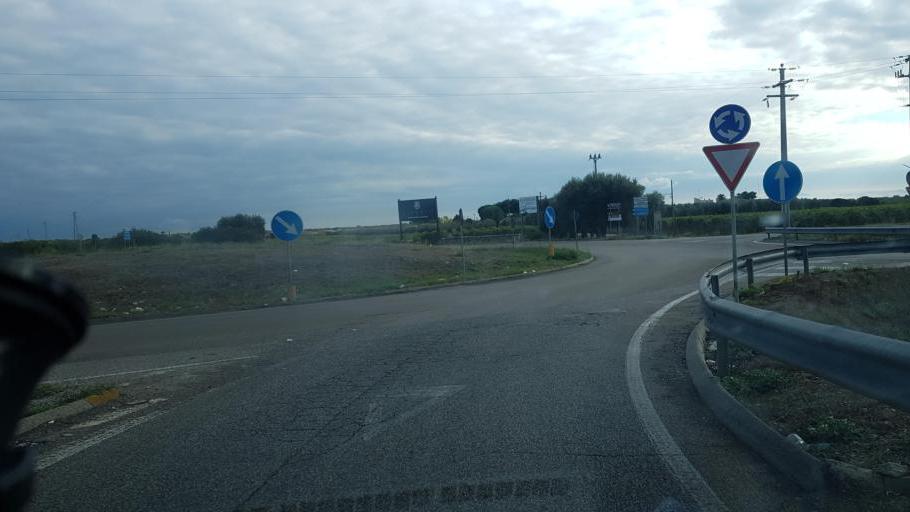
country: IT
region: Apulia
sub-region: Provincia di Brindisi
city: Francavilla Fontana
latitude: 40.5323
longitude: 17.5286
